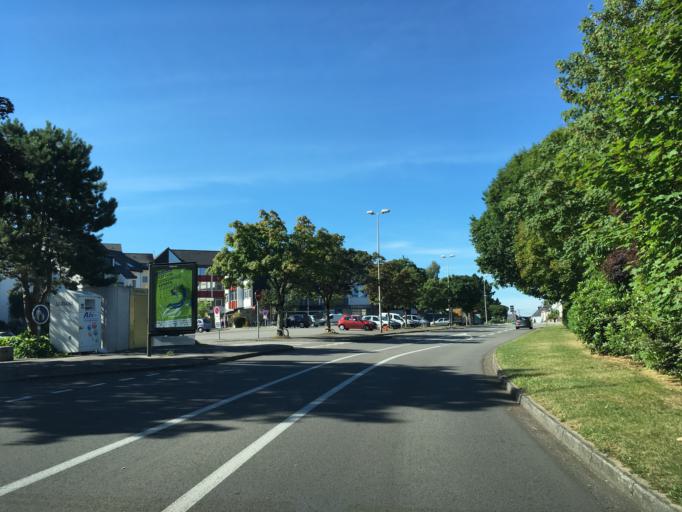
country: FR
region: Brittany
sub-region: Departement du Finistere
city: Quimper
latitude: 47.9852
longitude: -4.0834
